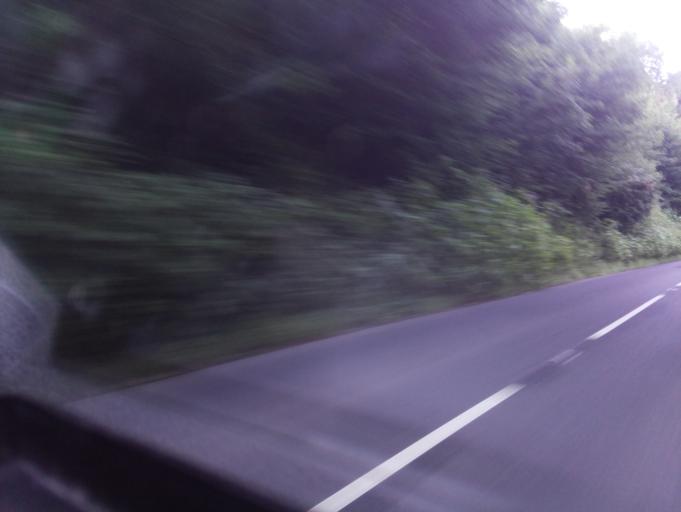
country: GB
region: Wales
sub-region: Monmouthshire
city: Monmouth
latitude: 51.7782
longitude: -2.6745
